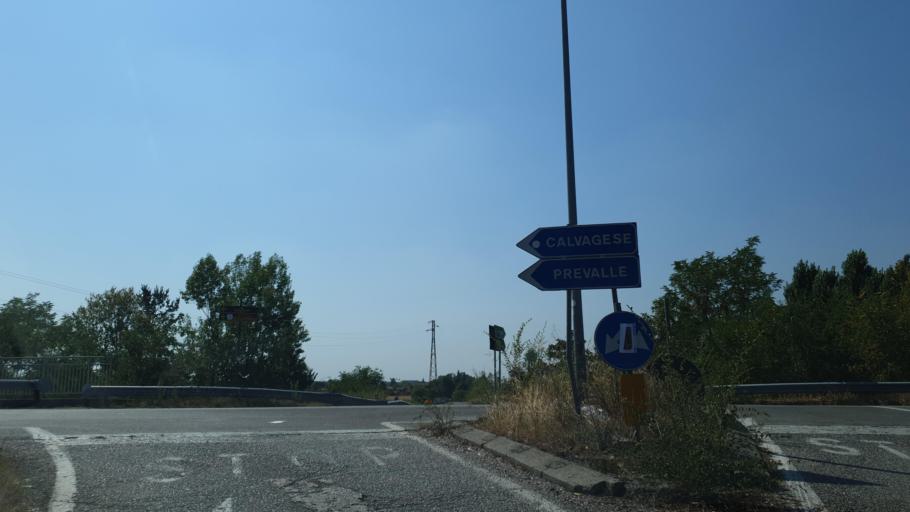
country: IT
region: Lombardy
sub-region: Provincia di Brescia
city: Prevalle
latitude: 45.5515
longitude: 10.4315
